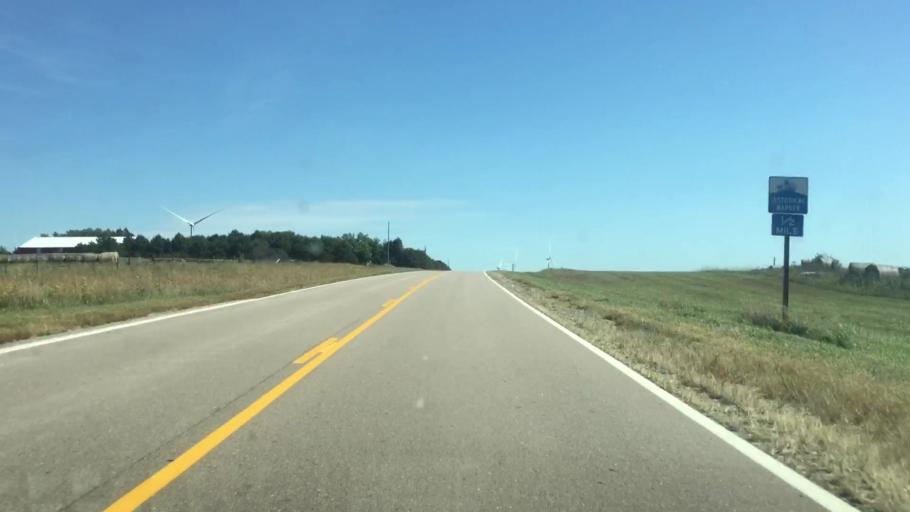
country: US
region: Kansas
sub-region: Washington County
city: Washington
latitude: 40.0453
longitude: -96.9447
